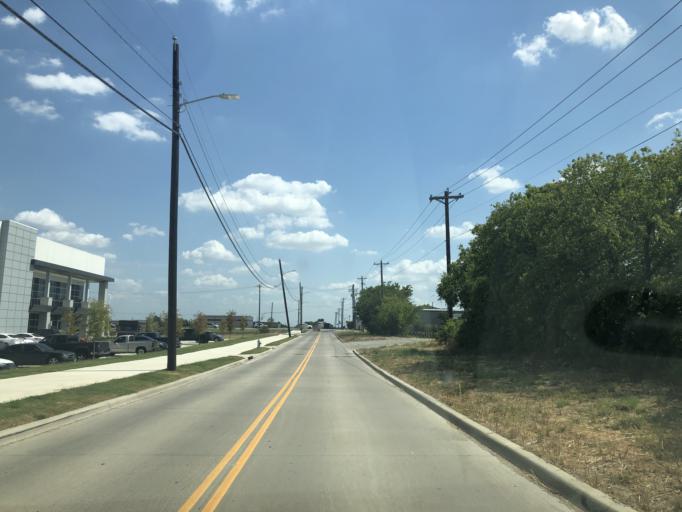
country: US
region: Texas
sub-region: Tarrant County
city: Haslet
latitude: 32.9353
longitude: -97.3228
